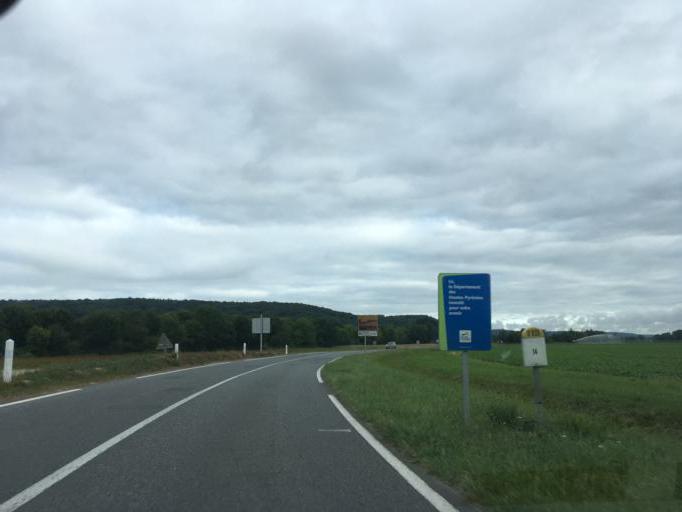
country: FR
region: Midi-Pyrenees
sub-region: Departement des Hautes-Pyrenees
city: Maubourguet
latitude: 43.4861
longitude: 0.0155
